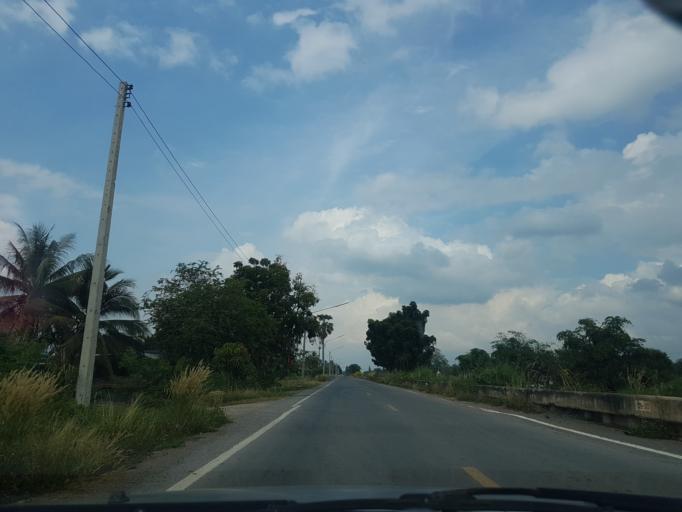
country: TH
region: Pathum Thani
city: Nong Suea
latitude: 14.2047
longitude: 100.8915
